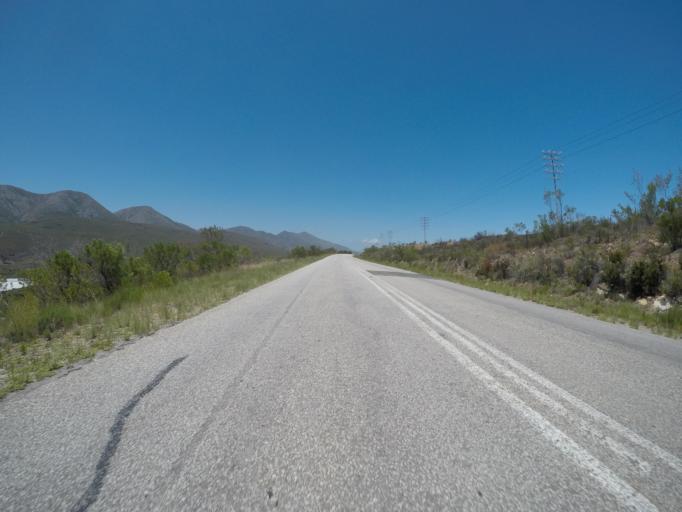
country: ZA
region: Eastern Cape
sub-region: Cacadu District Municipality
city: Kareedouw
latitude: -33.8944
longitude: 24.1070
